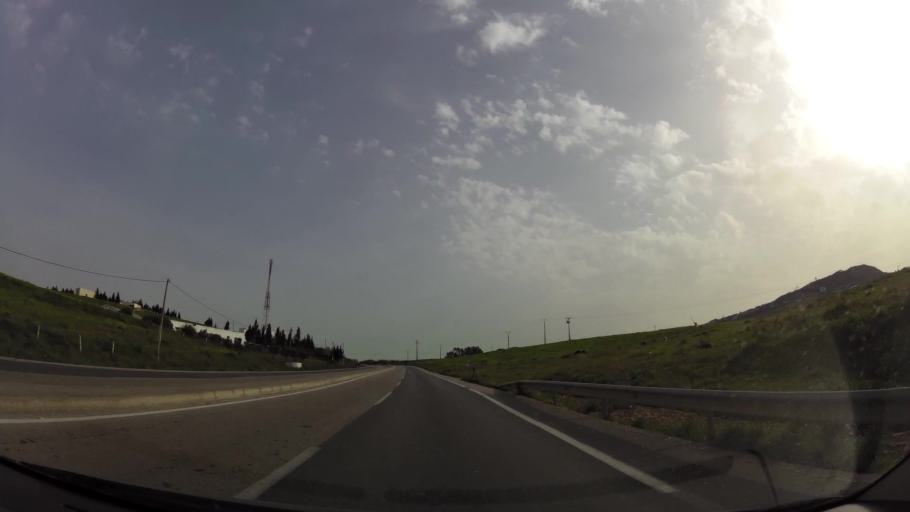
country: MA
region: Tanger-Tetouan
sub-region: Tanger-Assilah
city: Dar Chaoui
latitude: 35.6640
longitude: -5.6977
